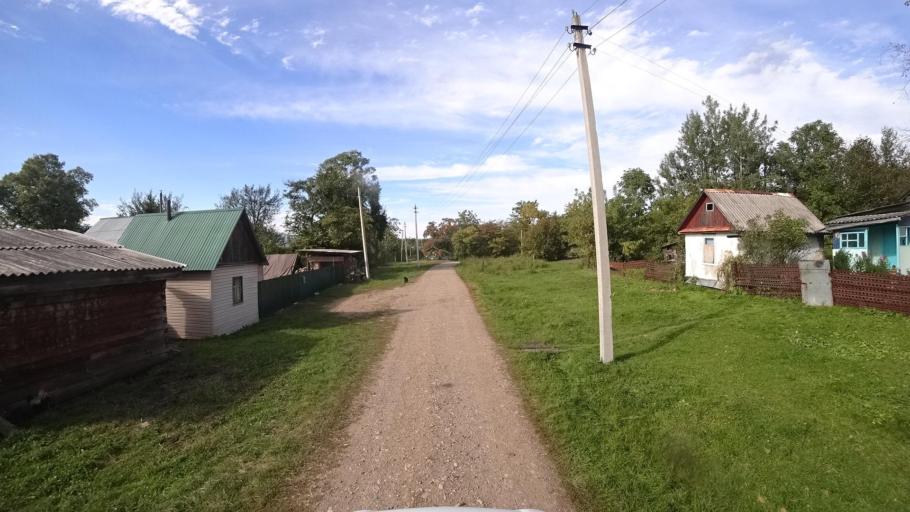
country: RU
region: Primorskiy
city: Dostoyevka
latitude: 44.2925
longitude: 133.4487
